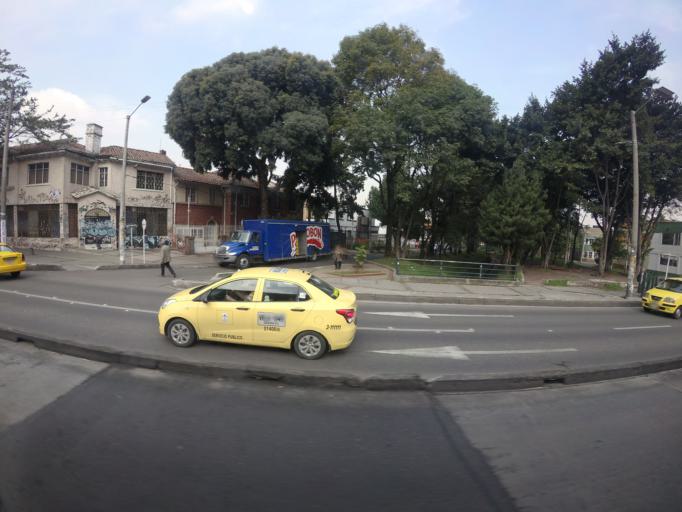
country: CO
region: Bogota D.C.
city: Bogota
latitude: 4.6289
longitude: -74.0685
